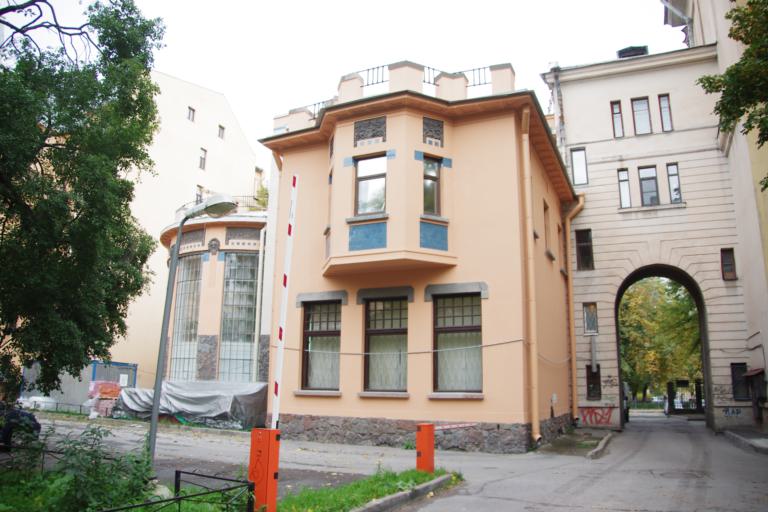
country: RU
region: St.-Petersburg
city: Petrogradka
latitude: 59.9637
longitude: 30.3226
